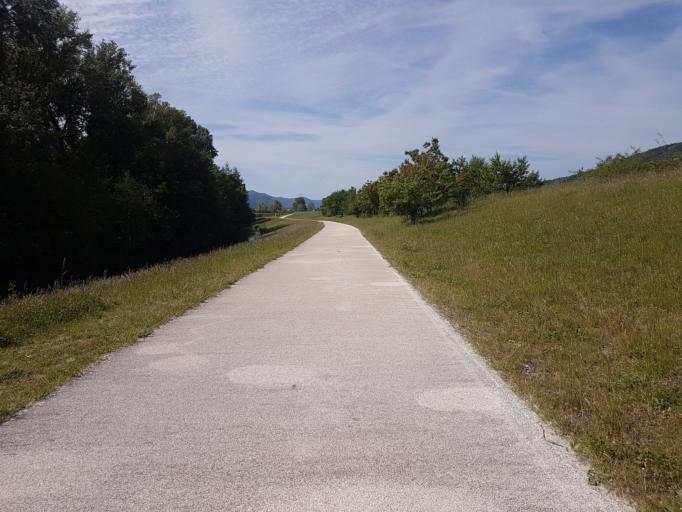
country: FR
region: Rhone-Alpes
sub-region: Departement de l'Ardeche
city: Le Pouzin
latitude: 44.7599
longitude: 4.7561
